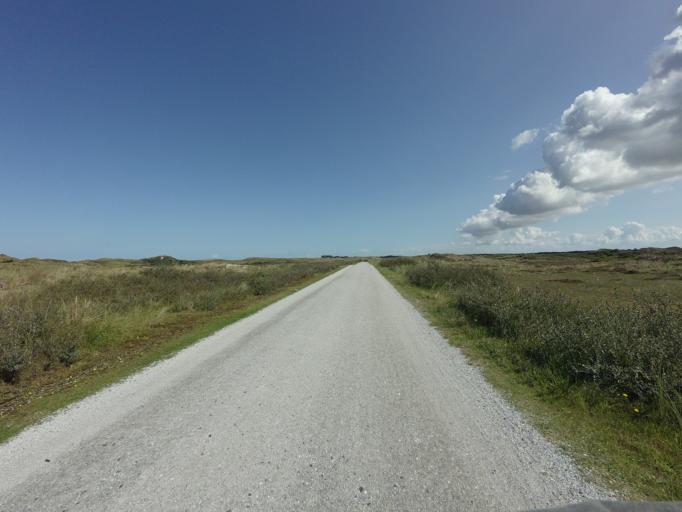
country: NL
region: Friesland
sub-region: Gemeente Terschelling
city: West-Terschelling
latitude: 53.3928
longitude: 5.2399
